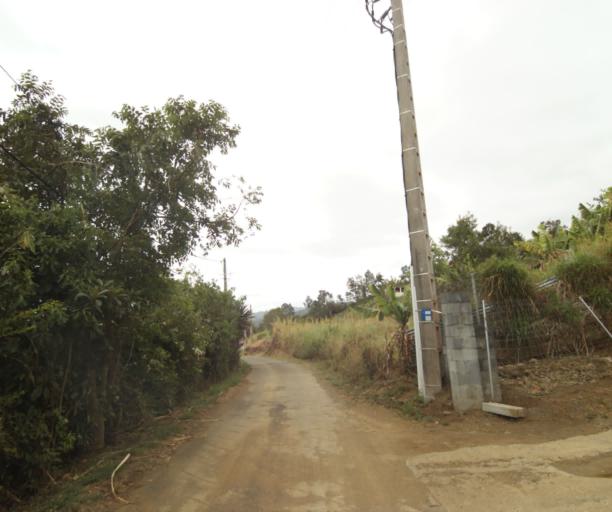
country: RE
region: Reunion
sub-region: Reunion
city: Saint-Paul
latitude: -21.0142
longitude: 55.3353
